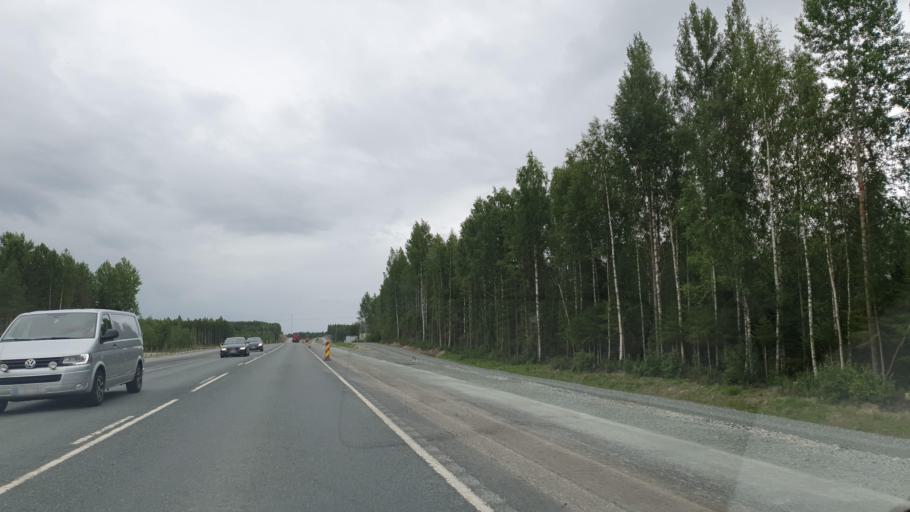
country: FI
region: Northern Savo
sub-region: Ylae-Savo
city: Lapinlahti
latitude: 63.2936
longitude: 27.4534
